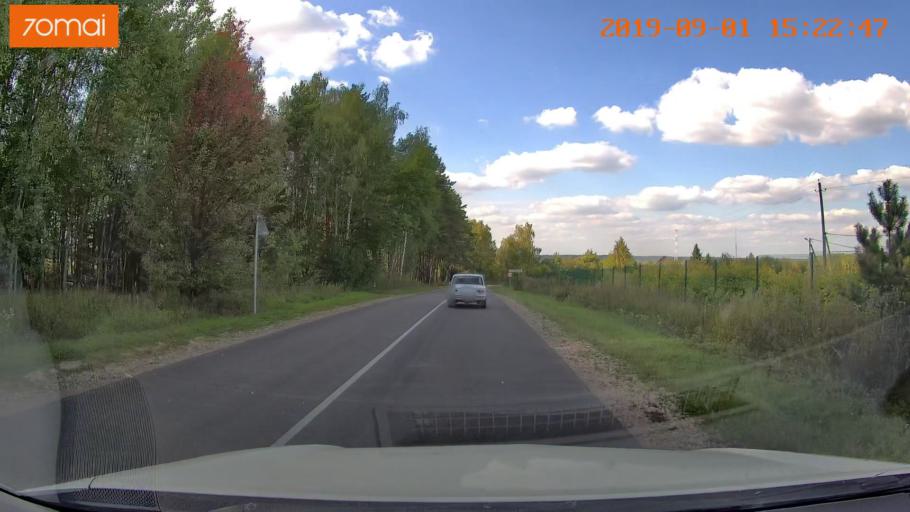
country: RU
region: Kaluga
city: Maloyaroslavets
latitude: 54.9393
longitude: 36.4610
